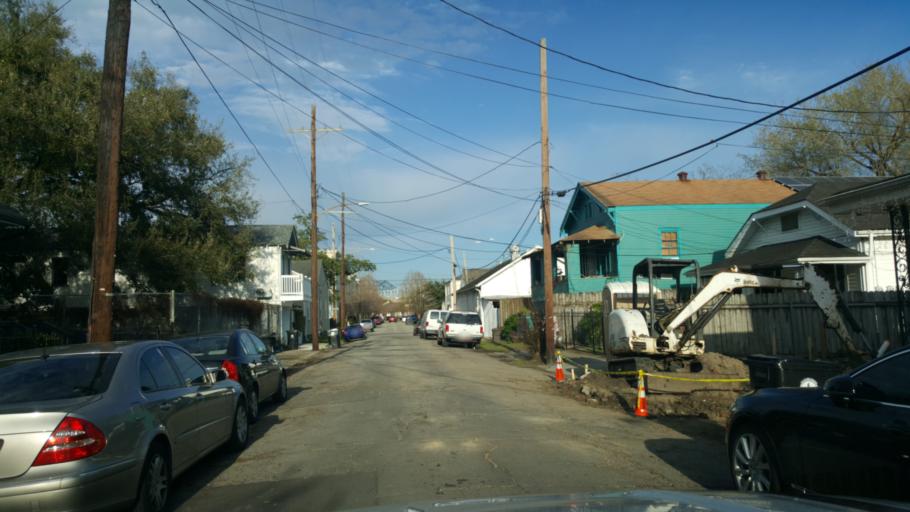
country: US
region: Louisiana
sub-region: Jefferson Parish
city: Harvey
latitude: 29.9282
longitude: -90.0751
